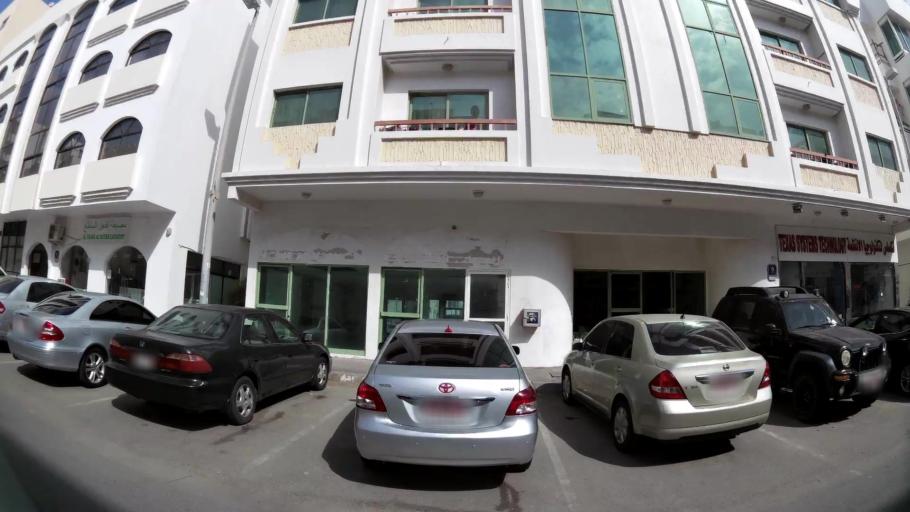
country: AE
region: Abu Dhabi
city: Abu Dhabi
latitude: 24.3345
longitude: 54.5333
